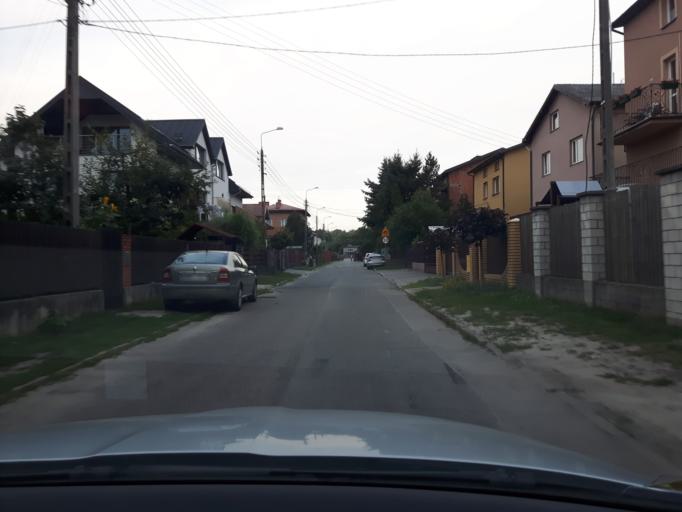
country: PL
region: Masovian Voivodeship
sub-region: Powiat wolominski
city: Zabki
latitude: 52.2917
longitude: 21.1048
